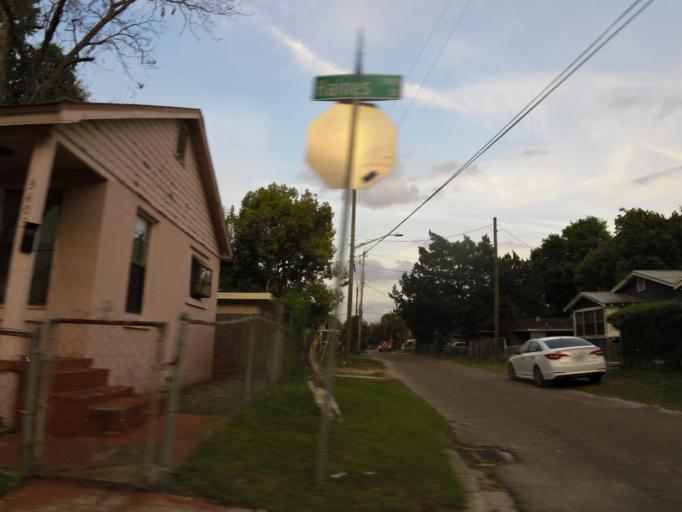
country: US
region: Florida
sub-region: Duval County
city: Jacksonville
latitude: 30.3596
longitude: -81.6370
